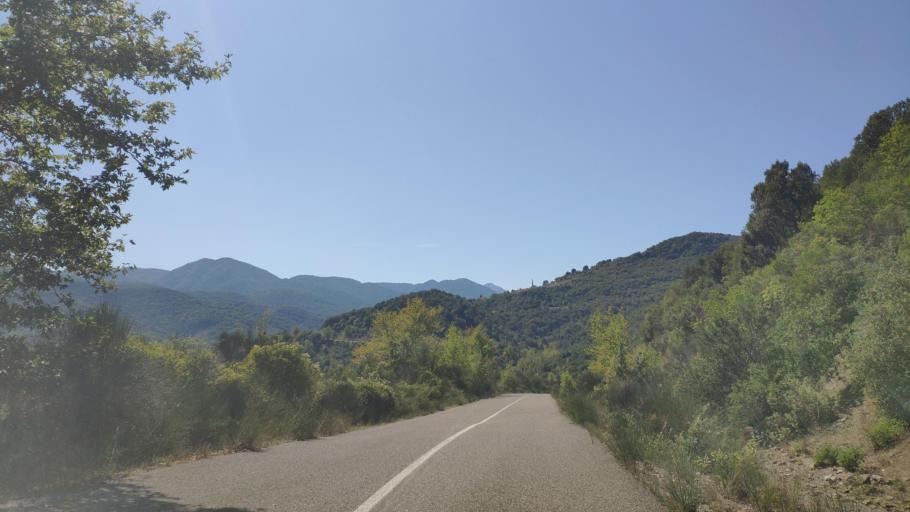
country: GR
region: Central Greece
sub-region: Nomos Evrytanias
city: Kerasochori
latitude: 38.9974
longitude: 21.5557
